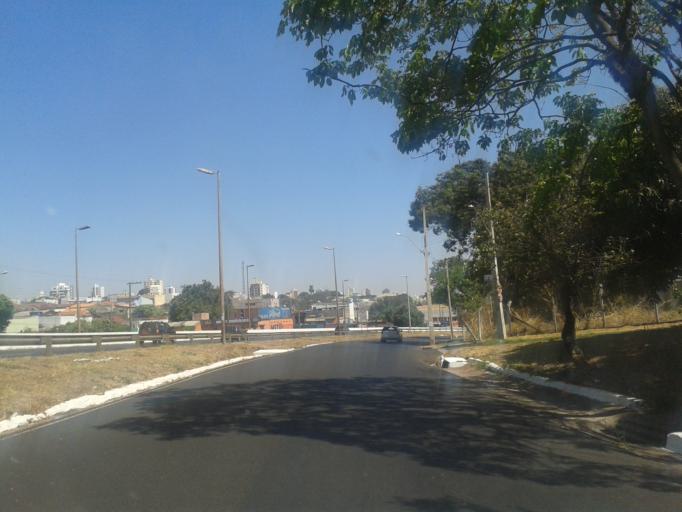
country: BR
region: Minas Gerais
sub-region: Uberlandia
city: Uberlandia
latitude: -18.8973
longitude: -48.2716
